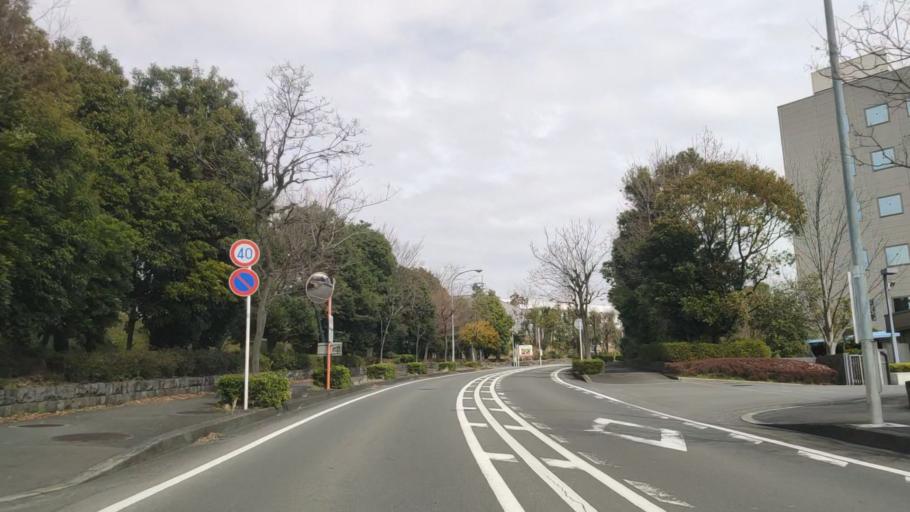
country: JP
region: Kanagawa
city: Hadano
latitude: 35.3468
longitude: 139.2219
